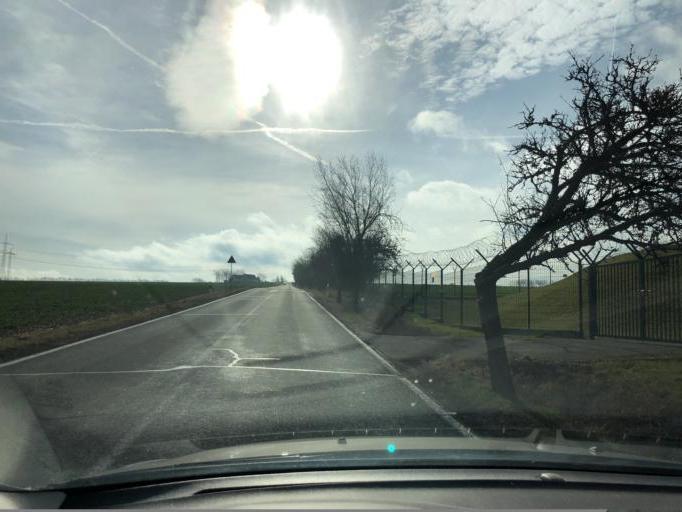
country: DE
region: Thuringia
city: Ballstedt
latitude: 51.0463
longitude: 11.2185
